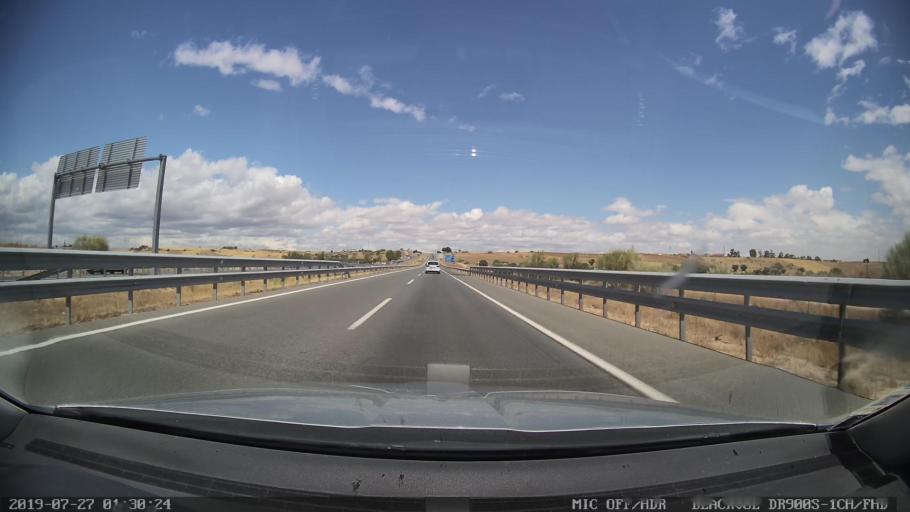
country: ES
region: Castille-La Mancha
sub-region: Province of Toledo
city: Valmojado
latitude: 40.1976
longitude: -4.1050
